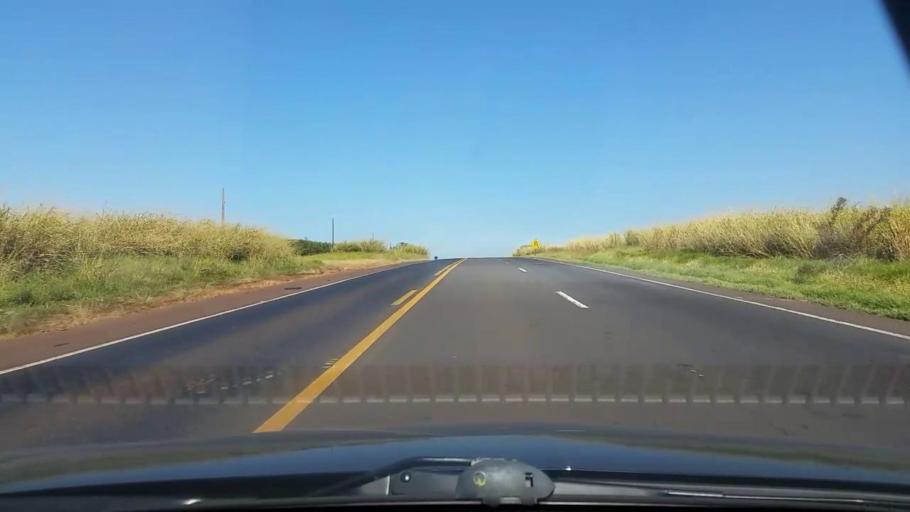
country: BR
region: Sao Paulo
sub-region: Jau
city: Jau
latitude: -22.3538
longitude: -48.5725
